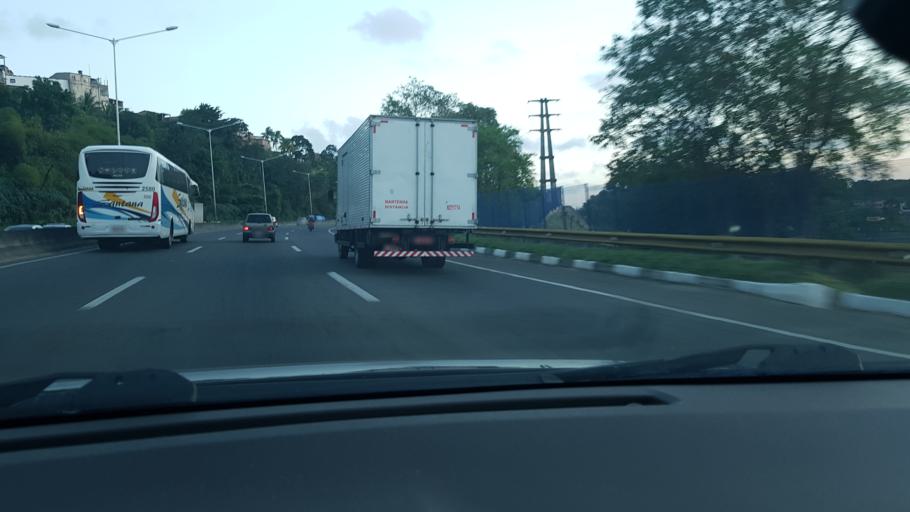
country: BR
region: Bahia
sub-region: Salvador
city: Salvador
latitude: -12.9466
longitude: -38.4699
